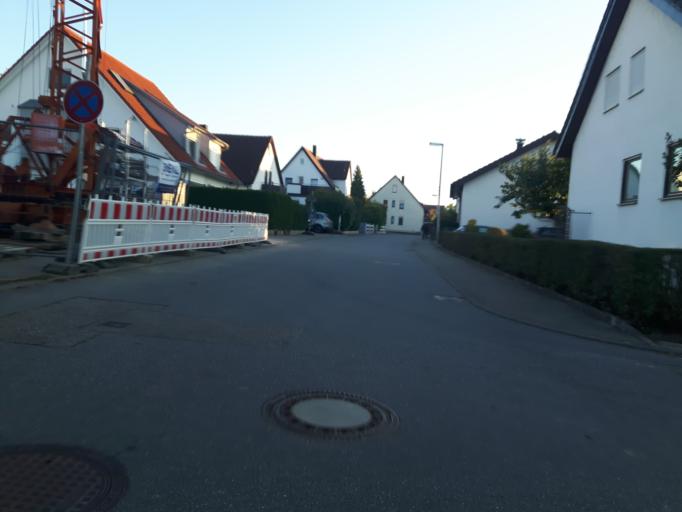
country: DE
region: Baden-Wuerttemberg
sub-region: Regierungsbezirk Stuttgart
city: Untereisesheim
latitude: 49.1997
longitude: 9.2020
